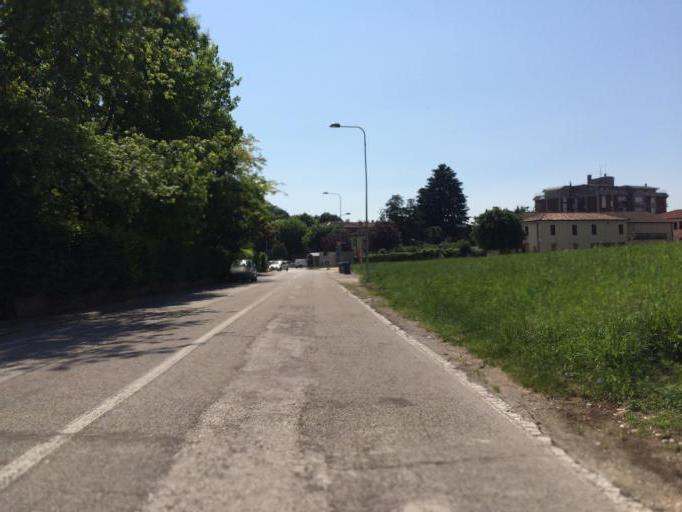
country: IT
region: Veneto
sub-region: Provincia di Vicenza
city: Montegalda
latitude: 45.4456
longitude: 11.6735
